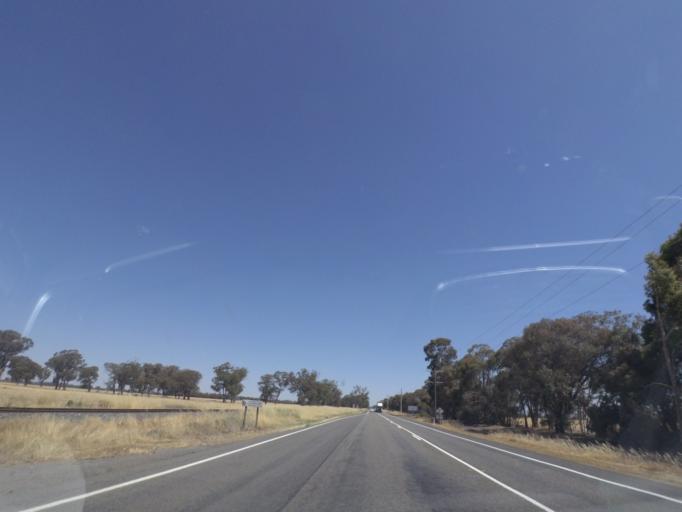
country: AU
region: Victoria
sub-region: Greater Shepparton
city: Shepparton
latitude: -36.1994
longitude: 145.4318
